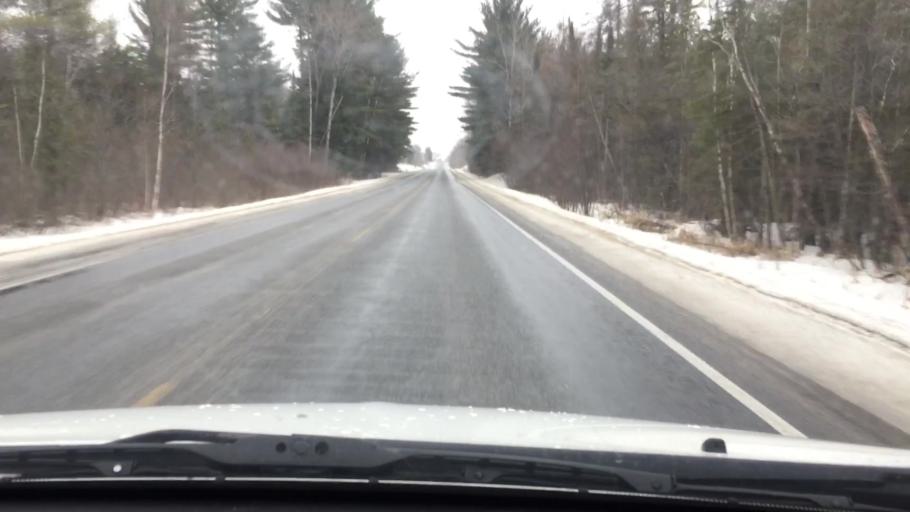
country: US
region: Michigan
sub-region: Osceola County
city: Reed City
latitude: 44.0550
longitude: -85.4439
